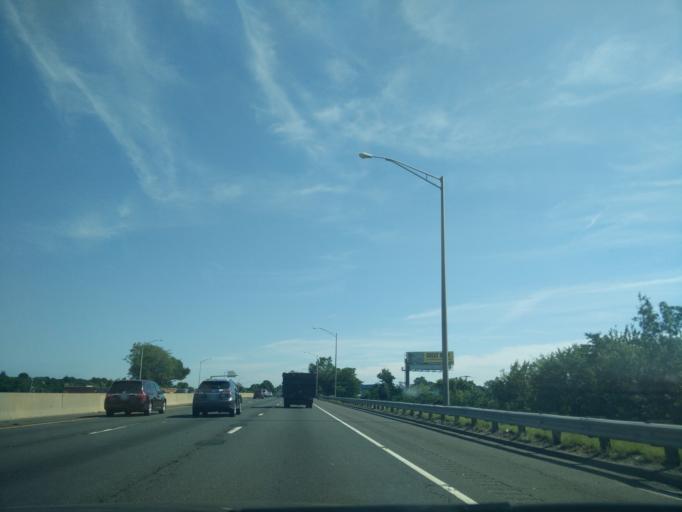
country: US
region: Connecticut
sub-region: Fairfield County
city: Stratford
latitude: 41.1774
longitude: -73.1491
